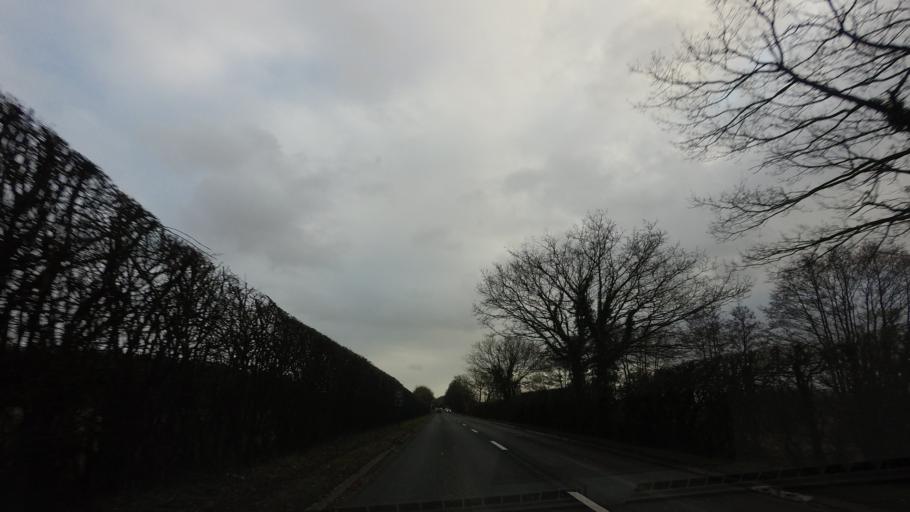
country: GB
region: England
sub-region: Kent
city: East Peckham
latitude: 51.2300
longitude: 0.3869
